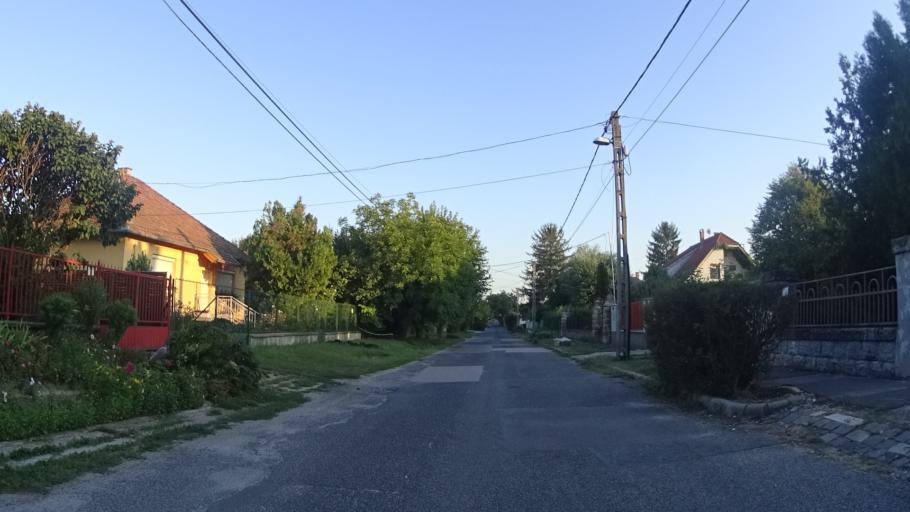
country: HU
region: Pest
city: Halasztelek
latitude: 47.3942
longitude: 19.0058
